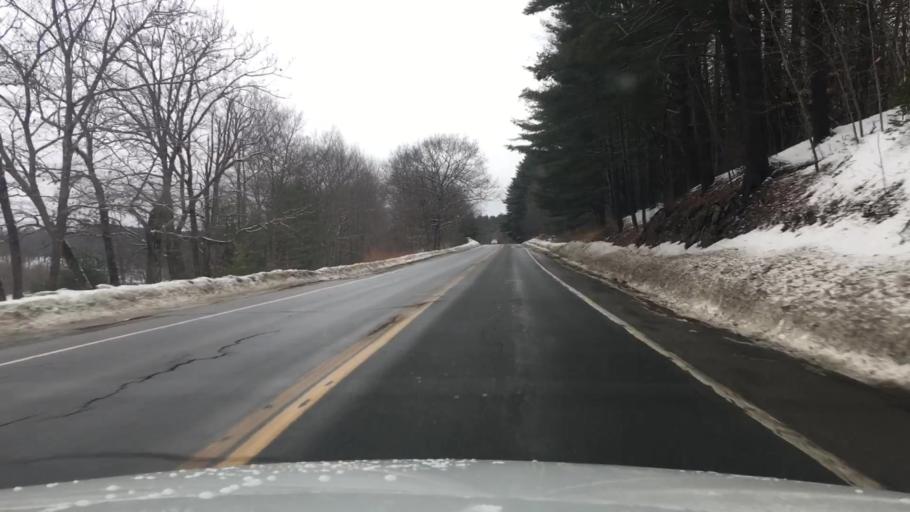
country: US
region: Maine
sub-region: Somerset County
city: Skowhegan
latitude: 44.7696
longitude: -69.6999
